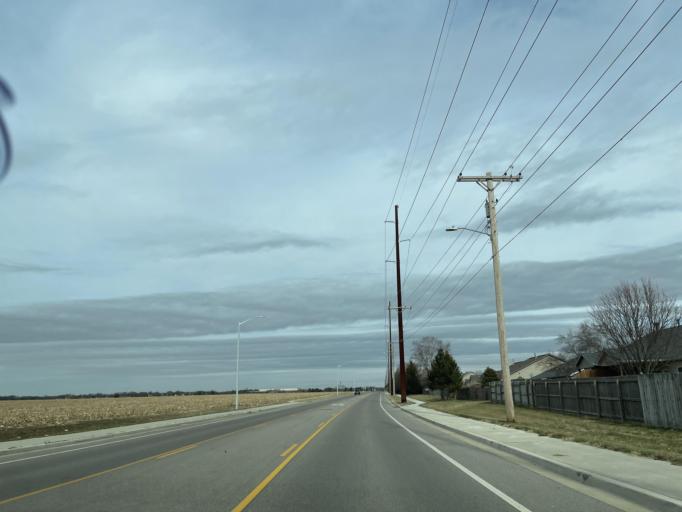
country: US
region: Illinois
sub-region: Sangamon County
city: Jerome
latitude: 39.7605
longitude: -89.7344
